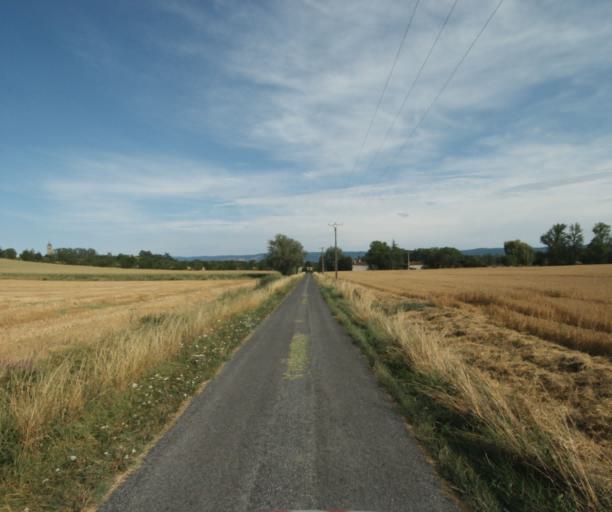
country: FR
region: Midi-Pyrenees
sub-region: Departement du Tarn
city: Puylaurens
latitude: 43.5268
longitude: 2.0001
